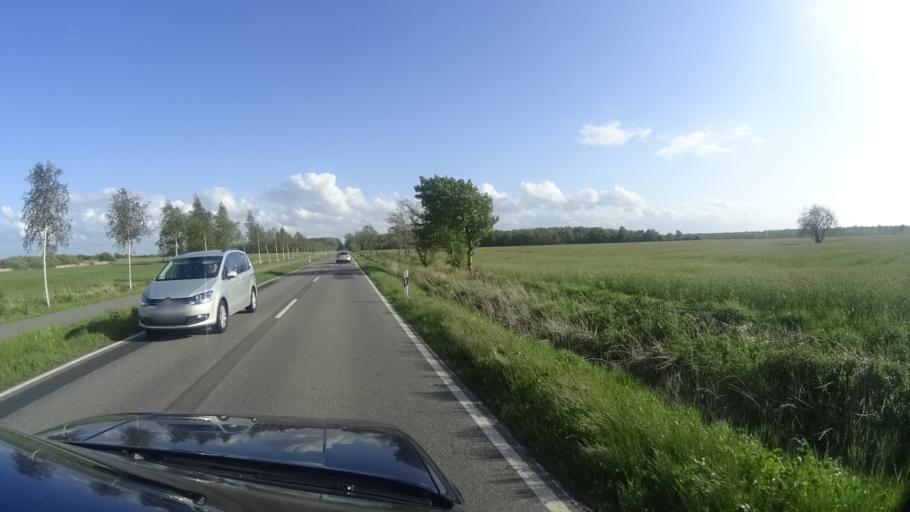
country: DE
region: Mecklenburg-Vorpommern
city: Ostseebad Dierhagen
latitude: 54.2861
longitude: 12.3544
